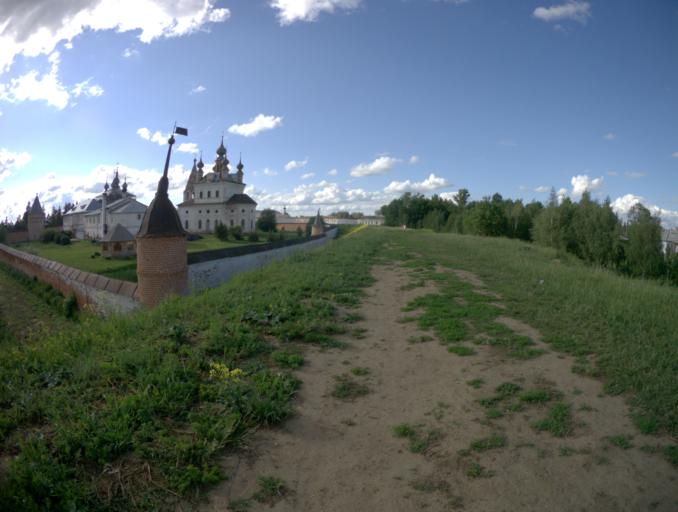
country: RU
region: Vladimir
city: Yur'yev-Pol'skiy
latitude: 56.4972
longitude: 39.6832
